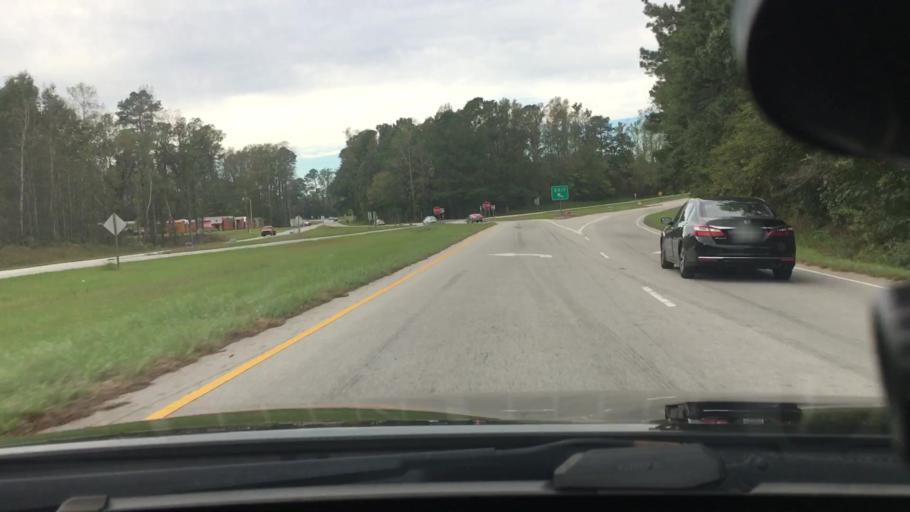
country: US
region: North Carolina
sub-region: Craven County
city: Vanceboro
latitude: 35.2871
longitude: -77.1282
